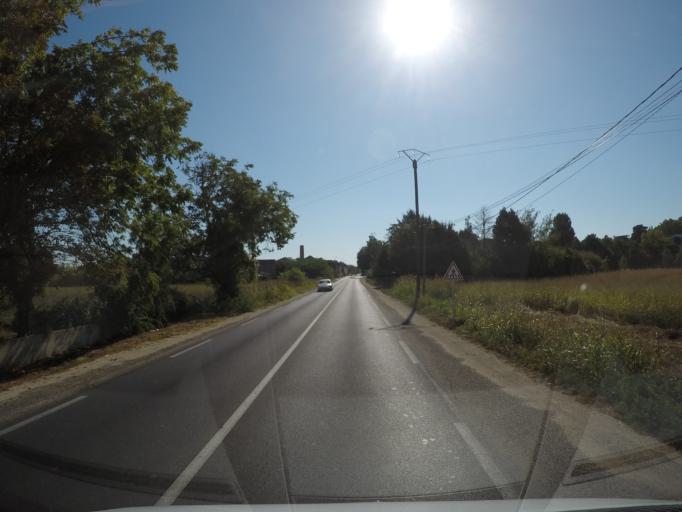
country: FR
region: Languedoc-Roussillon
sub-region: Departement du Gard
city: Moussac
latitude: 43.9761
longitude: 4.2118
